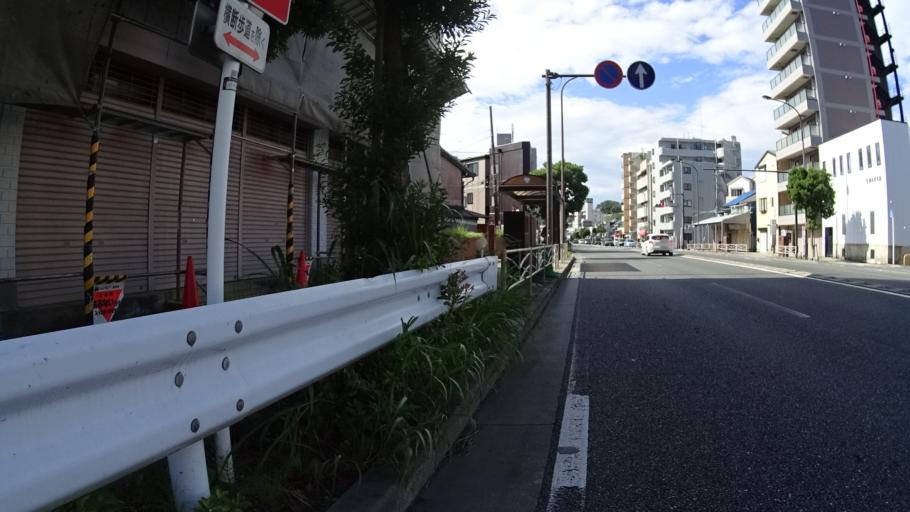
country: JP
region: Kanagawa
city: Yokosuka
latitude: 35.2757
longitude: 139.6771
